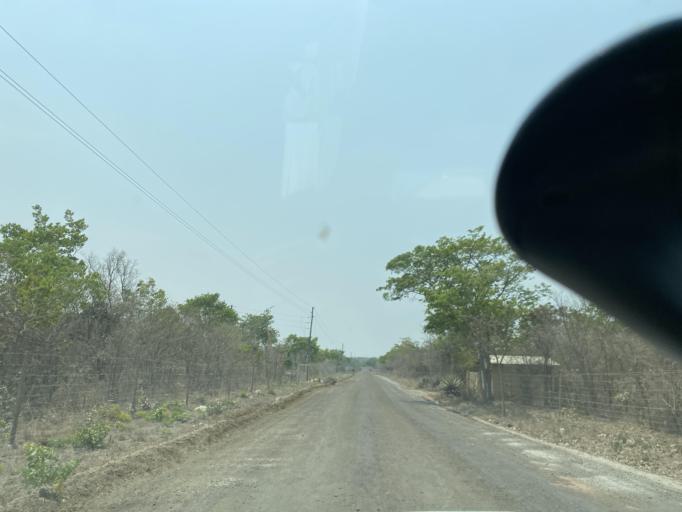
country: ZM
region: Lusaka
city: Lusaka
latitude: -15.5152
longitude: 28.4441
